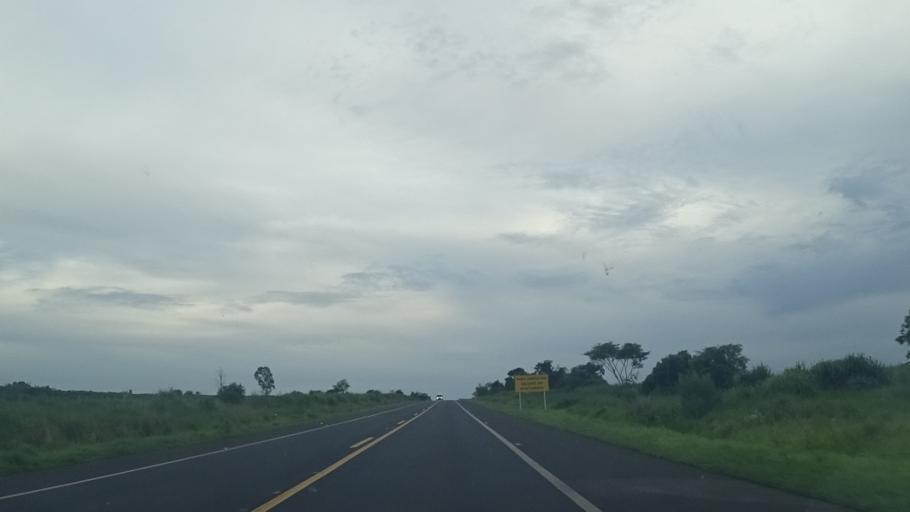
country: BR
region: Sao Paulo
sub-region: Martinopolis
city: Martinopolis
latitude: -22.1013
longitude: -51.1466
